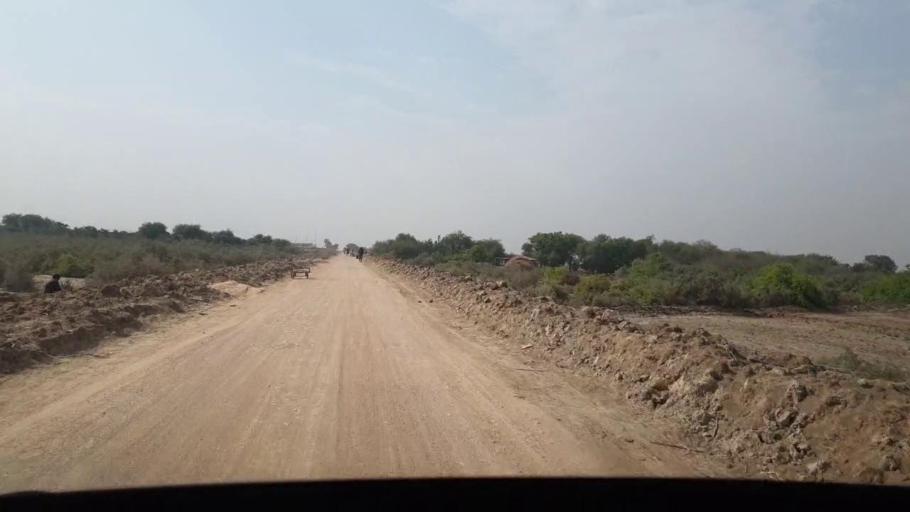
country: PK
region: Sindh
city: Chuhar Jamali
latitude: 24.3672
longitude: 67.9412
